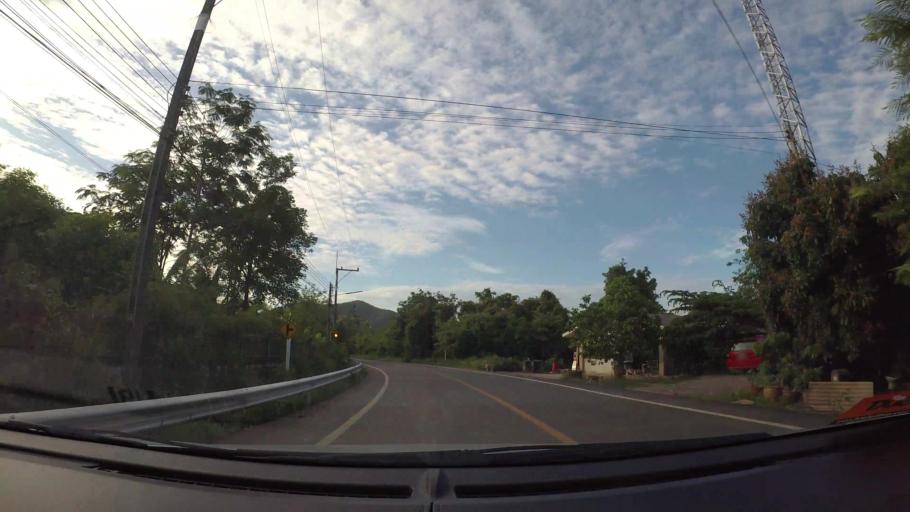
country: TH
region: Chon Buri
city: Sattahip
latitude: 12.7044
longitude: 100.9304
